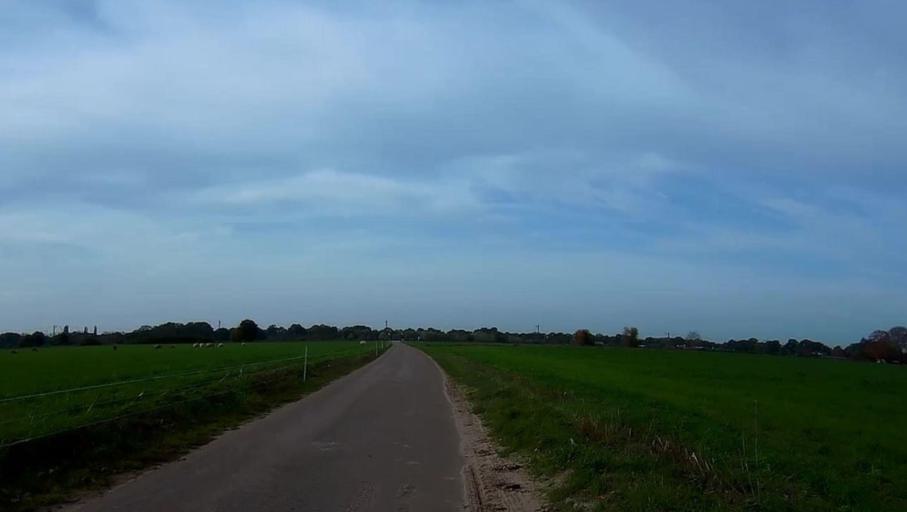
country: NL
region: Gelderland
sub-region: Gemeente Ede
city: Lunteren
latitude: 52.0683
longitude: 5.6506
